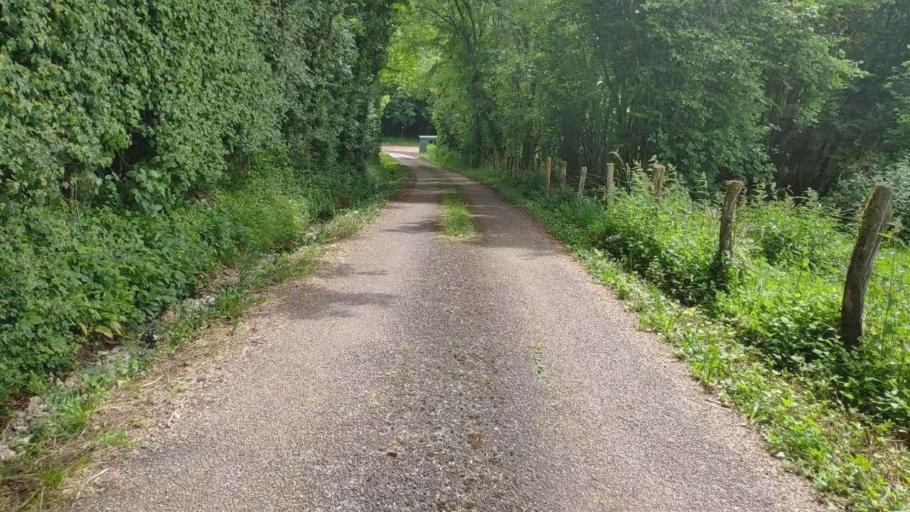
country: FR
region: Franche-Comte
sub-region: Departement du Jura
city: Montmorot
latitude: 46.7431
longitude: 5.5483
